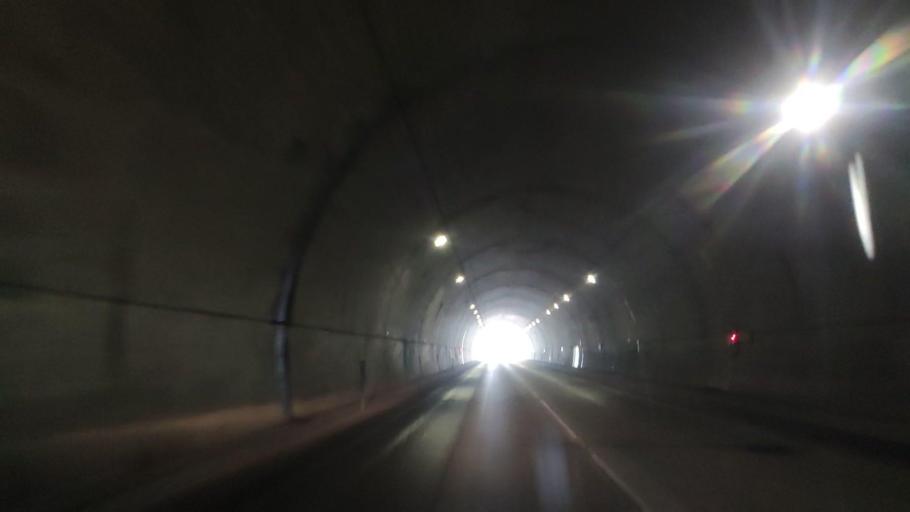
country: JP
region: Nagano
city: Iiyama
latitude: 36.8662
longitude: 138.3665
